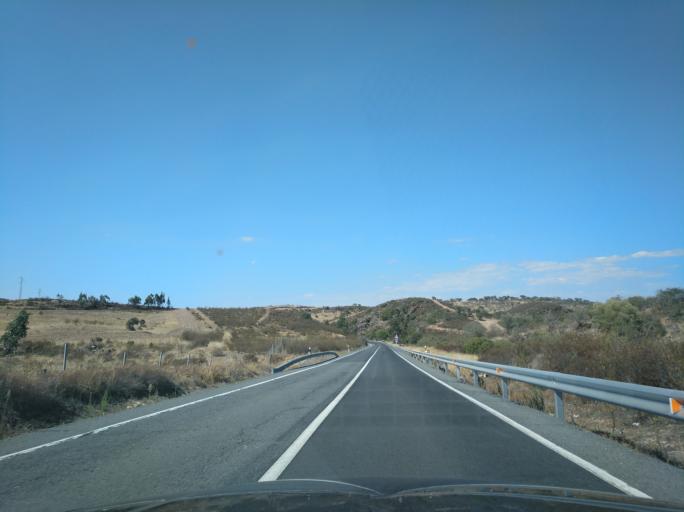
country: ES
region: Andalusia
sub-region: Provincia de Huelva
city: San Bartolome de la Torre
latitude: 37.4736
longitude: -7.1263
